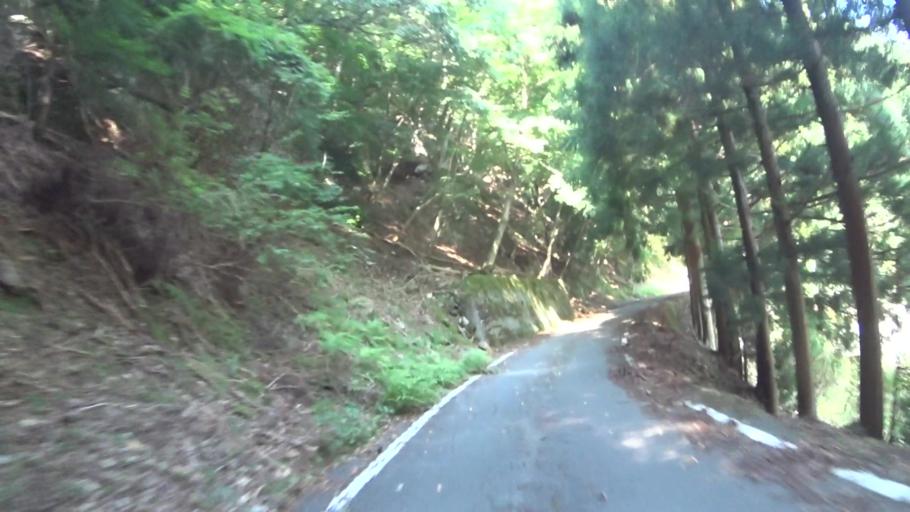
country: JP
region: Fukui
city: Obama
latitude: 35.2716
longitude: 135.6920
